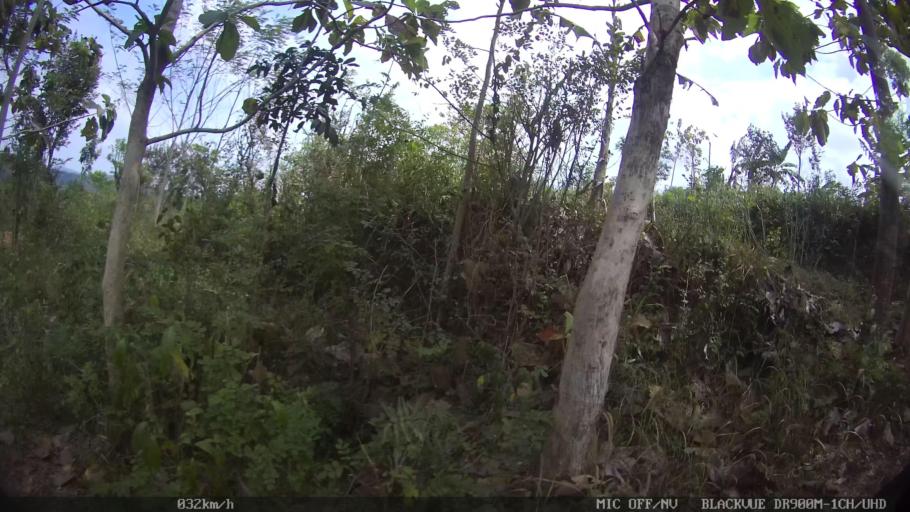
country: ID
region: Central Java
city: Candi Prambanan
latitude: -7.8153
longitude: 110.5249
